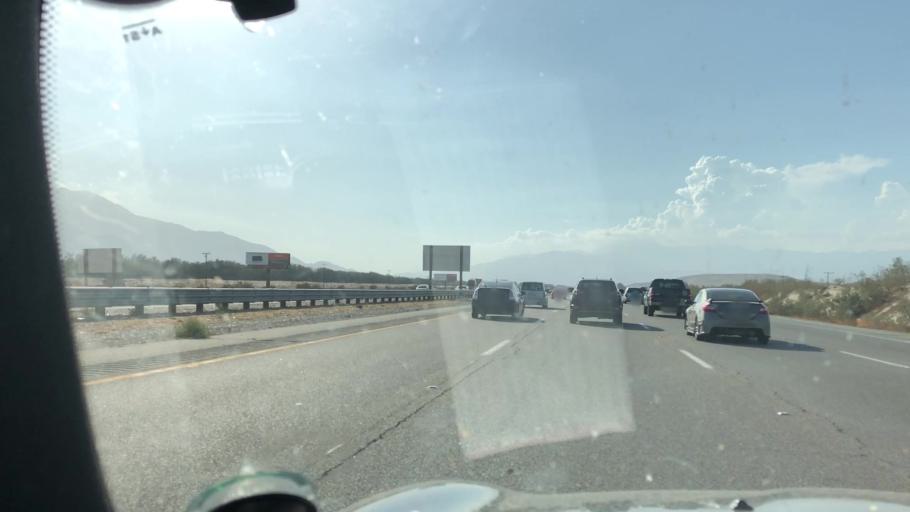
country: US
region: California
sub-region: Riverside County
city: Thousand Palms
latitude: 33.8282
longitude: -116.4224
